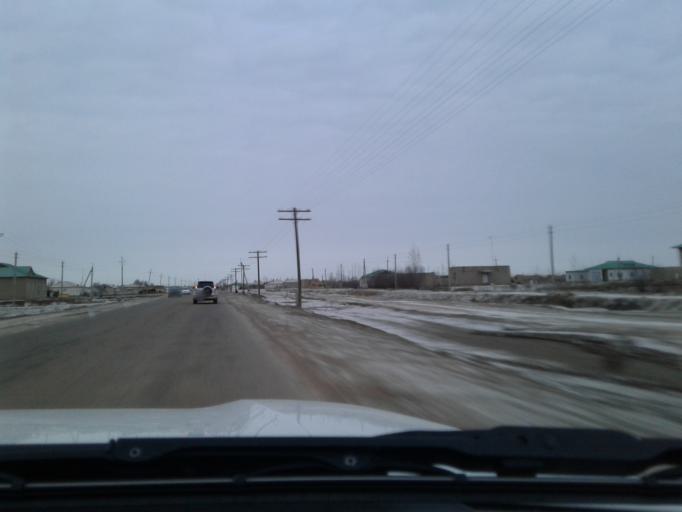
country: TM
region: Dasoguz
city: Dasoguz
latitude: 42.0044
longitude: 59.8797
